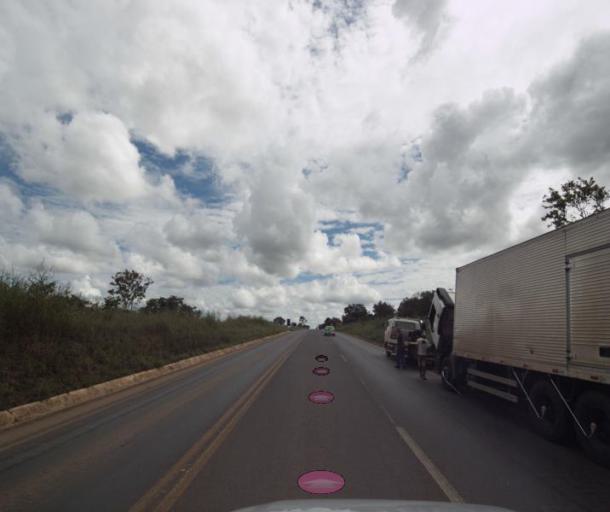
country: BR
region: Goias
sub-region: Uruacu
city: Uruacu
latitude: -14.4815
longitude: -49.1540
